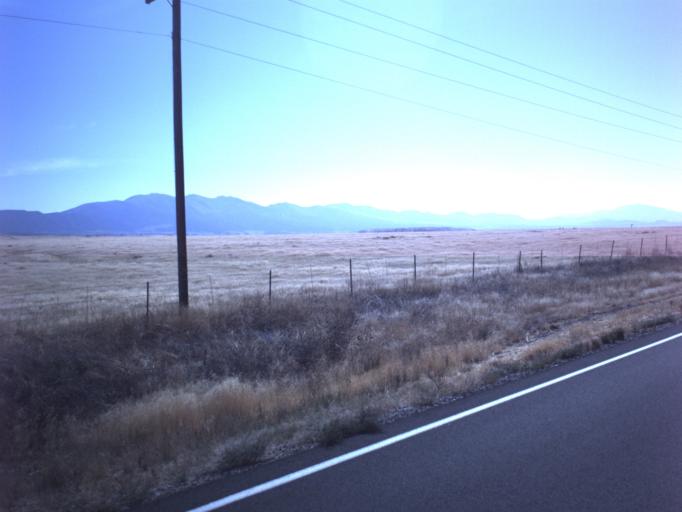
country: US
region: Utah
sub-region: Tooele County
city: Grantsville
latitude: 40.3875
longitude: -112.7473
